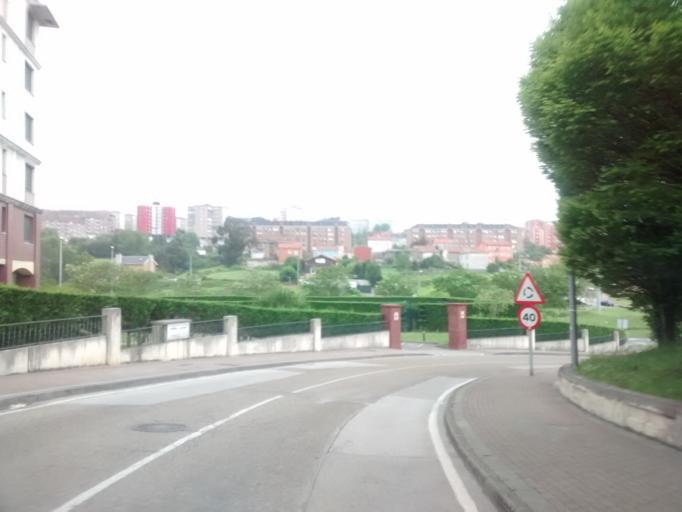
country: ES
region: Cantabria
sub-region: Provincia de Cantabria
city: Santander
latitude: 43.4693
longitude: -3.8247
